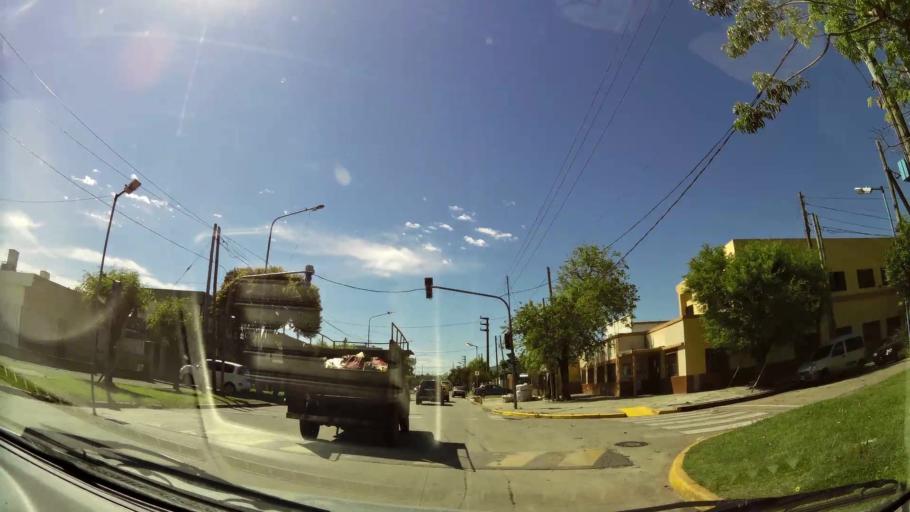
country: AR
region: Buenos Aires
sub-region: Partido de Quilmes
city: Quilmes
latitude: -34.7002
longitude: -58.2855
